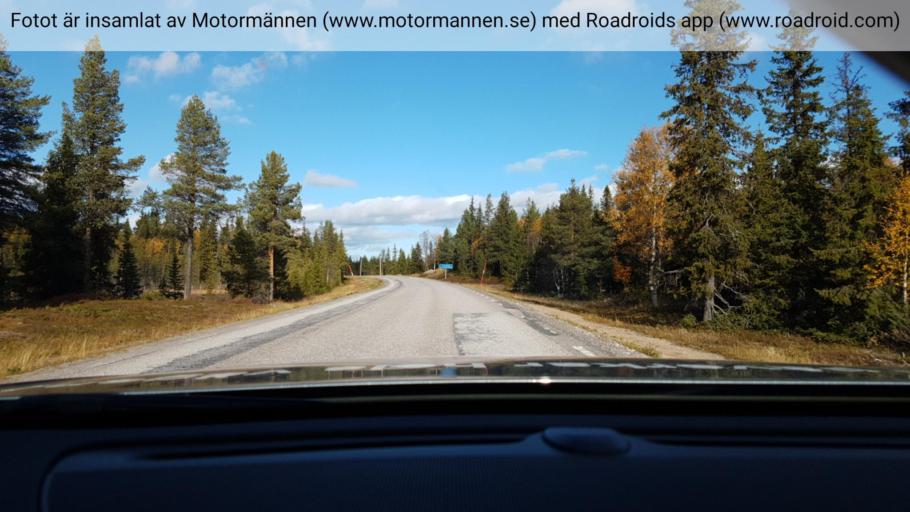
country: SE
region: Norrbotten
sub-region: Arjeplogs Kommun
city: Arjeplog
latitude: 65.8769
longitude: 18.4065
